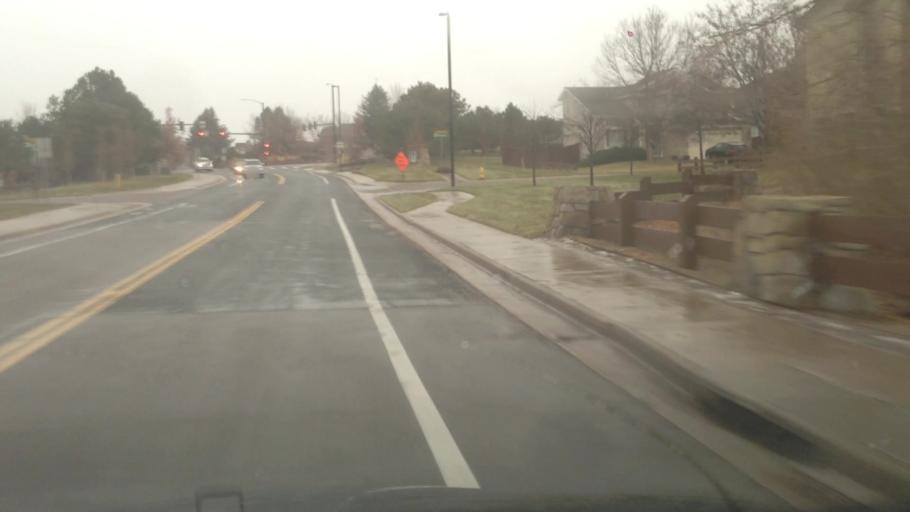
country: US
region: Colorado
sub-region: Douglas County
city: Stonegate
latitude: 39.5242
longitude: -104.7954
